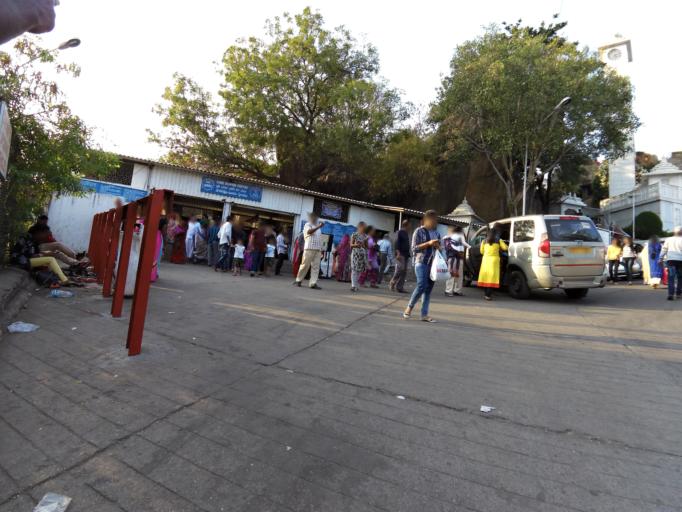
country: IN
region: Telangana
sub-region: Hyderabad
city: Hyderabad
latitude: 17.4053
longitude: 78.4693
